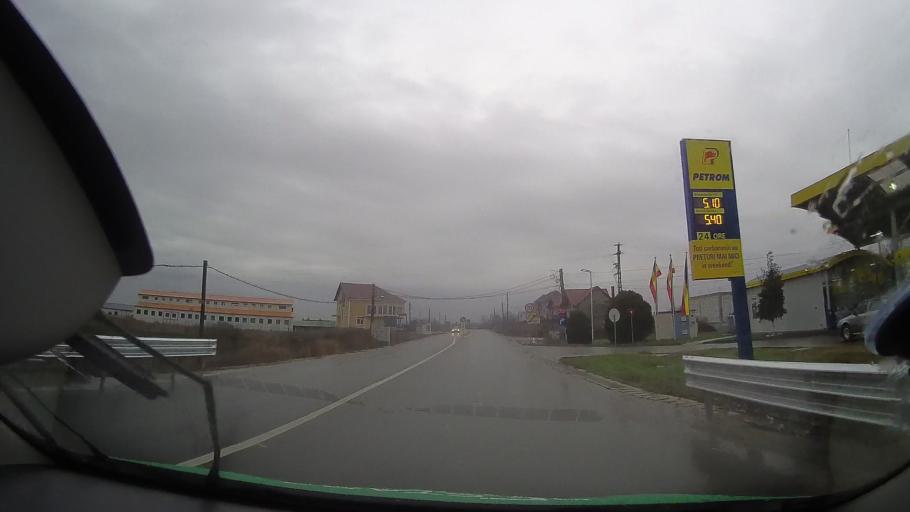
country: RO
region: Bihor
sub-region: Municipiul Beius
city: Beius
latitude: 46.6693
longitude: 22.3363
